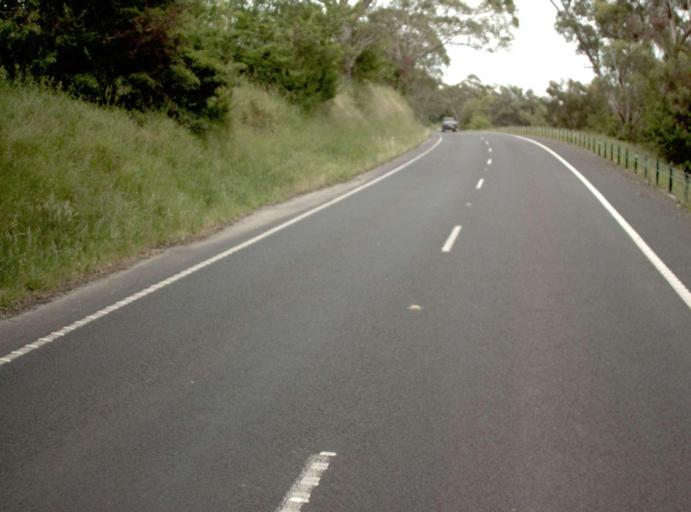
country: AU
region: Victoria
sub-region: Bass Coast
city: North Wonthaggi
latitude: -38.5827
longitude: 146.0010
